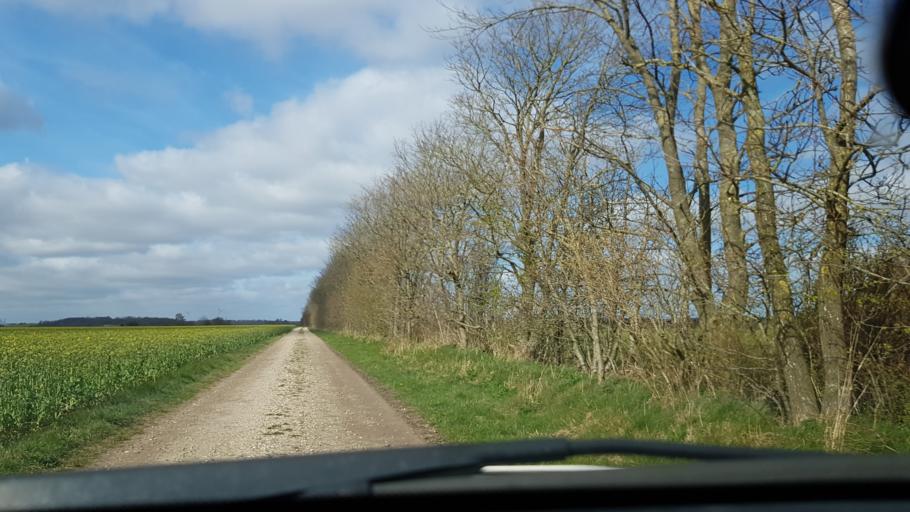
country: DK
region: South Denmark
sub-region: Vejen Kommune
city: Rodding
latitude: 55.3692
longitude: 8.9660
